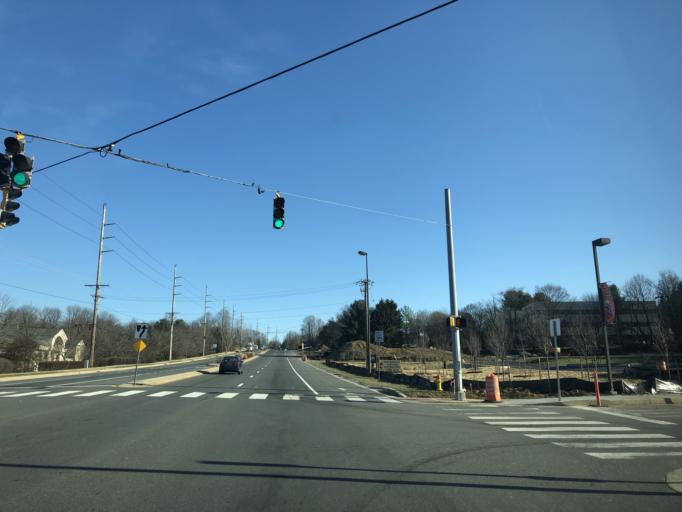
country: US
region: Delaware
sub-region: New Castle County
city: Hockessin
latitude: 39.7871
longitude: -75.6908
